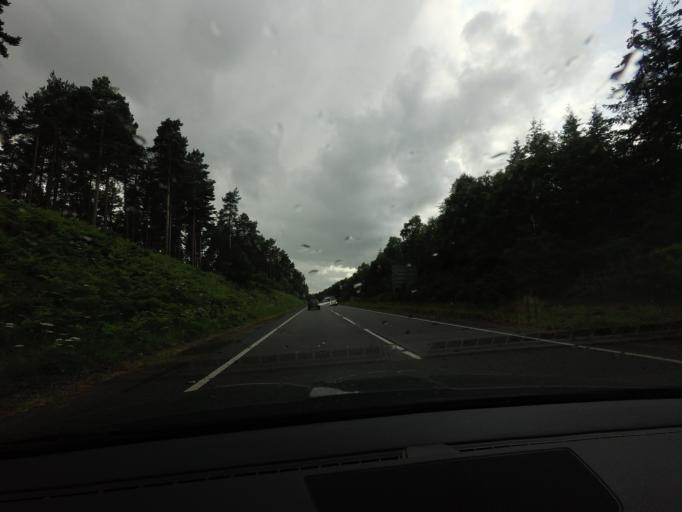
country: GB
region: Scotland
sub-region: Highland
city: Fortrose
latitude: 57.5298
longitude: -4.0503
